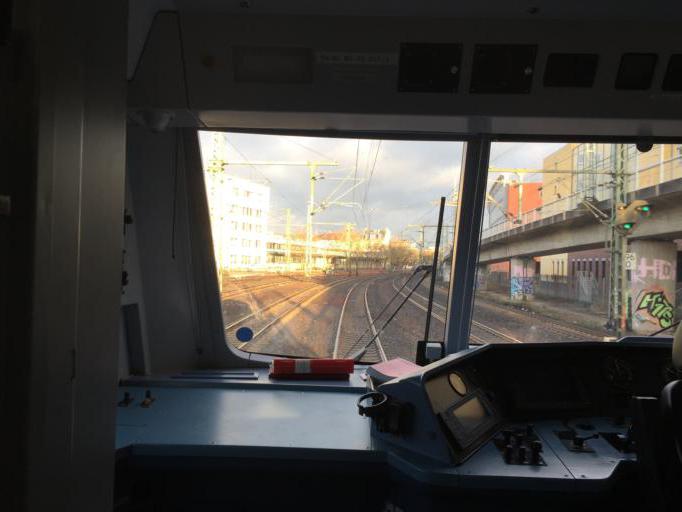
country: DE
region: Hesse
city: Niederrad
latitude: 50.1213
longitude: 8.6357
